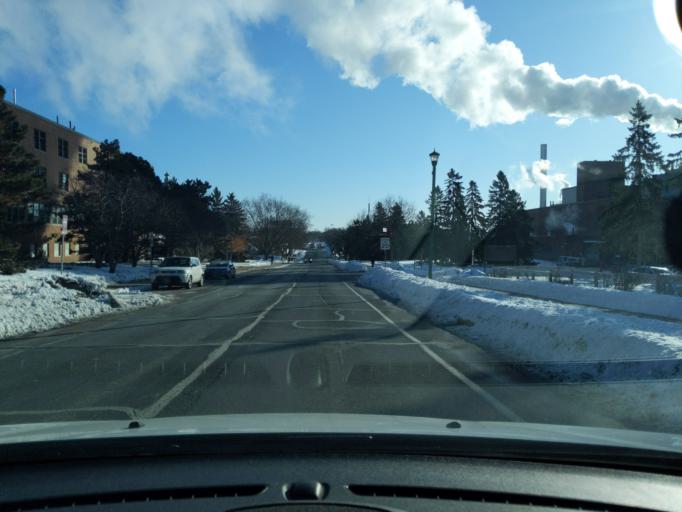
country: US
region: Minnesota
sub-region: Ramsey County
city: Falcon Heights
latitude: 44.9808
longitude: -93.1840
